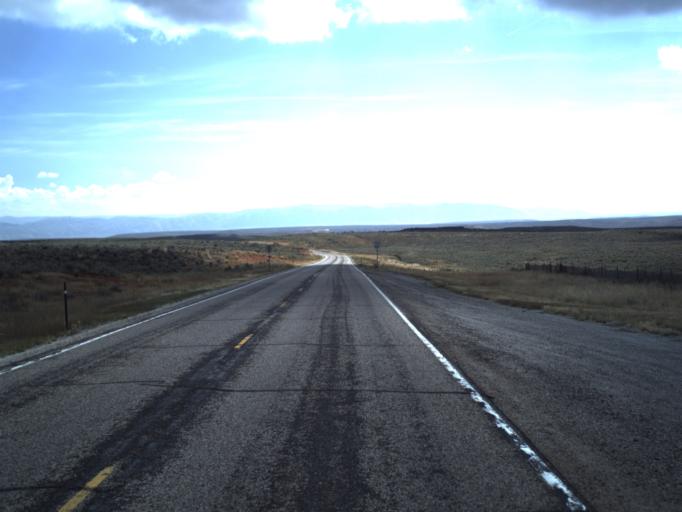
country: US
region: Utah
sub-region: Rich County
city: Randolph
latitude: 41.8048
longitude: -111.2475
